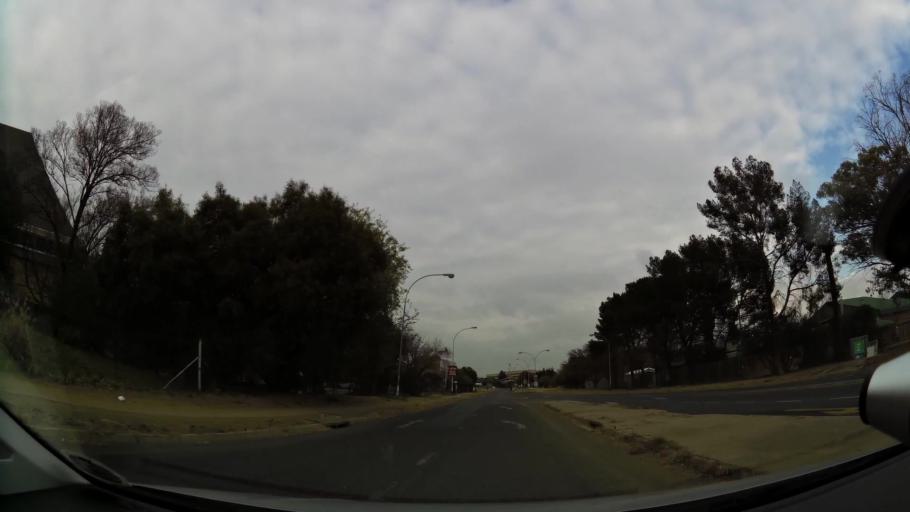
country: ZA
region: Orange Free State
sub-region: Mangaung Metropolitan Municipality
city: Bloemfontein
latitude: -29.1055
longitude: 26.1883
